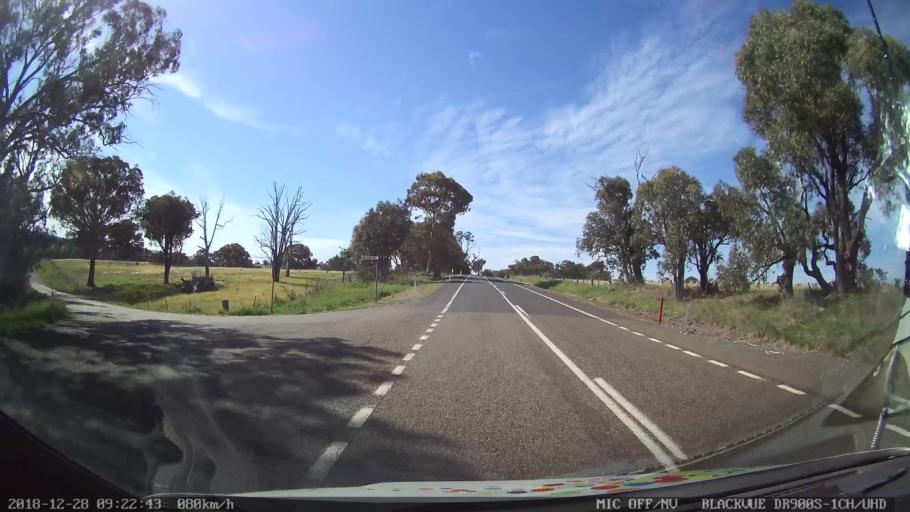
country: AU
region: New South Wales
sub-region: Upper Lachlan Shire
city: Crookwell
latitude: -34.3771
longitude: 149.3828
